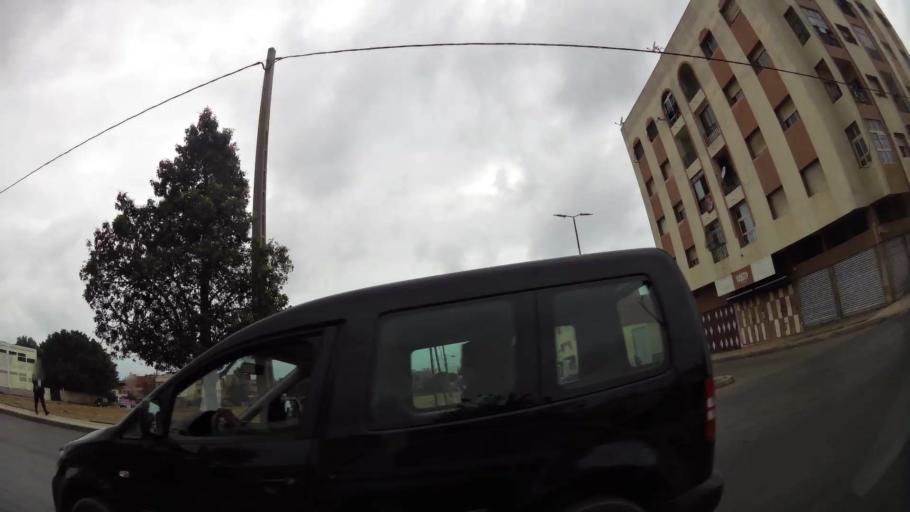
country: MA
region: Rabat-Sale-Zemmour-Zaer
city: Sale
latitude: 34.0434
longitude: -6.8019
